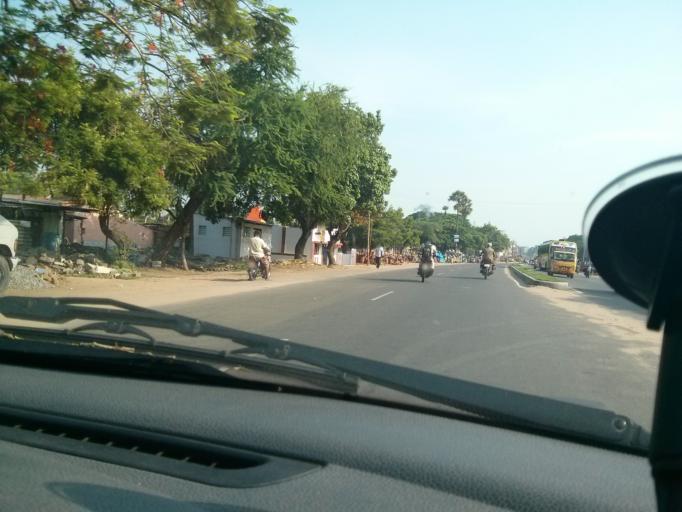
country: IN
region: Tamil Nadu
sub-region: Coimbatore
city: Coimbatore
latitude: 11.0382
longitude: 76.9499
